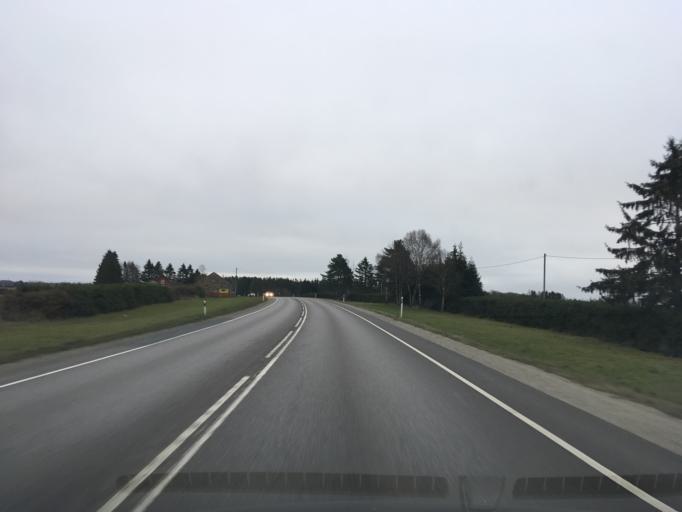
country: EE
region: Laeaene-Virumaa
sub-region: Rakvere linn
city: Rakvere
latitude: 59.4010
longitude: 26.3699
